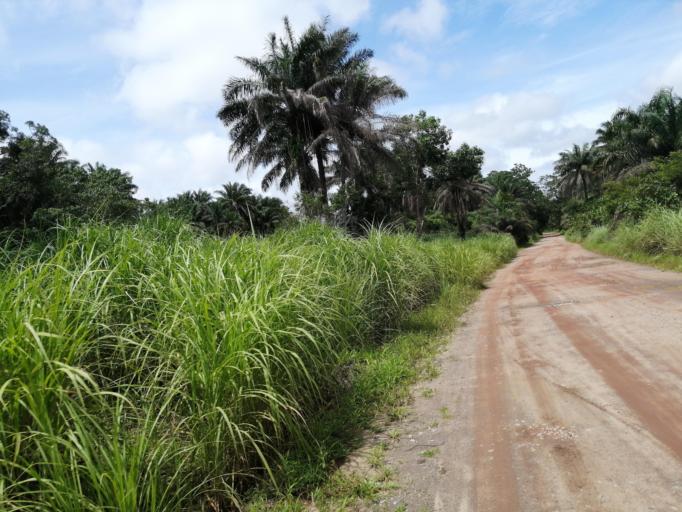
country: SL
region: Northern Province
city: Pepel
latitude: 8.6797
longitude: -12.9999
